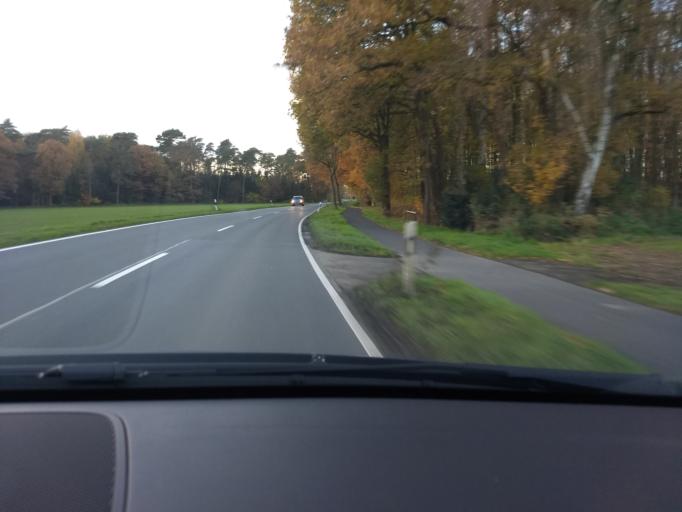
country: DE
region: North Rhine-Westphalia
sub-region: Regierungsbezirk Munster
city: Klein Reken
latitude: 51.7512
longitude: 7.0199
